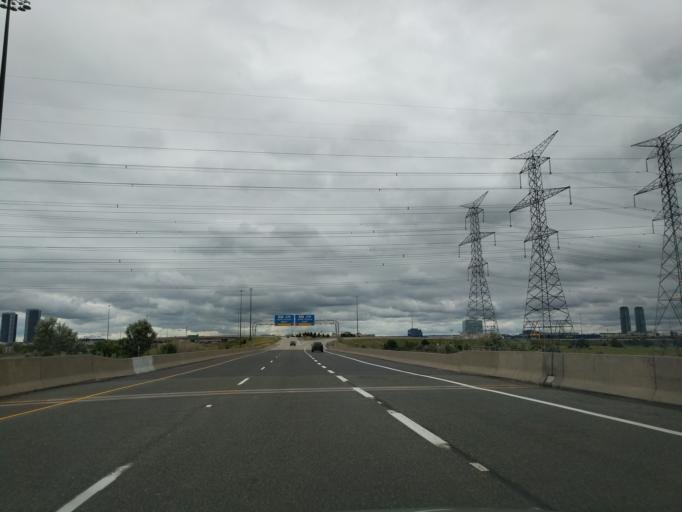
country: CA
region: Ontario
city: Concord
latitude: 43.7773
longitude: -79.5350
